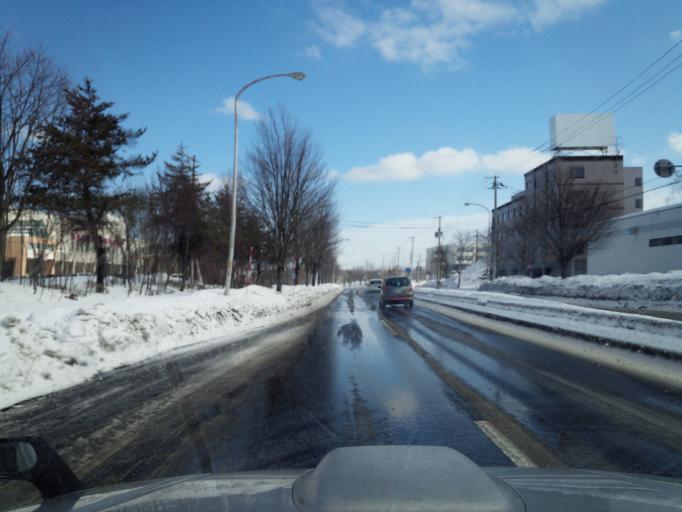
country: JP
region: Hokkaido
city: Kitahiroshima
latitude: 42.9959
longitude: 141.4588
